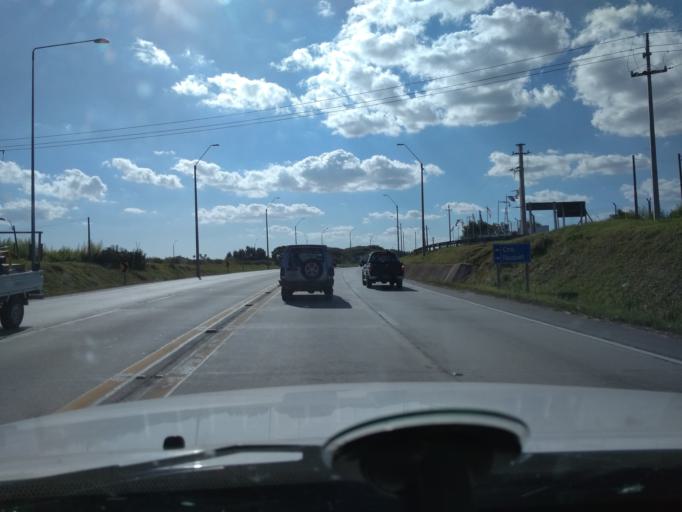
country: UY
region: Canelones
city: La Paz
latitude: -34.7832
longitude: -56.2498
